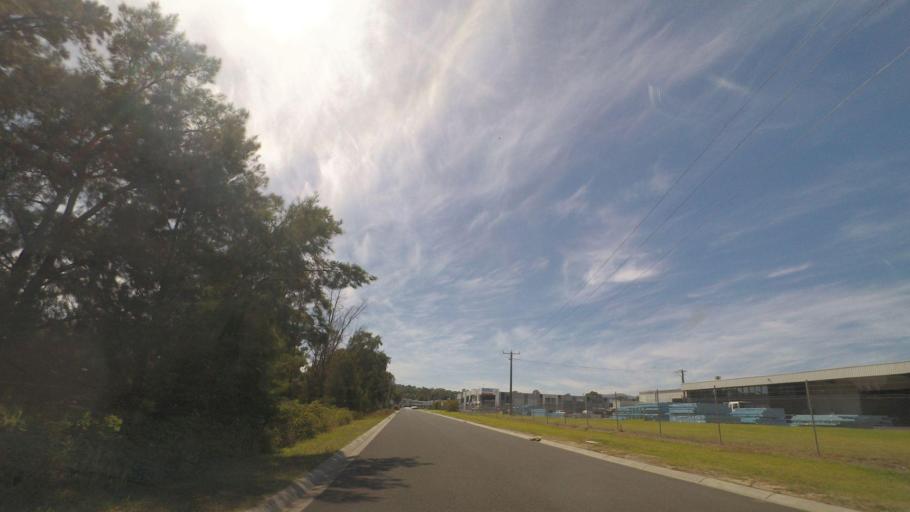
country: AU
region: Victoria
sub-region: Maroondah
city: Croydon North
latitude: -37.7696
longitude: 145.2995
